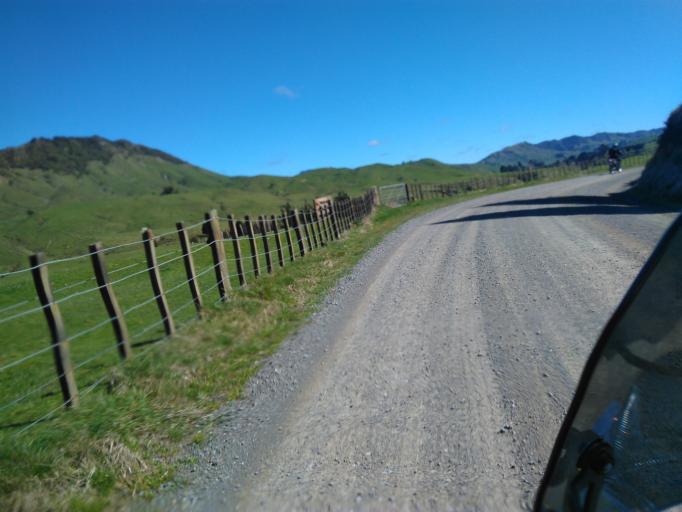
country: NZ
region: Bay of Plenty
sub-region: Opotiki District
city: Opotiki
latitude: -38.3088
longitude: 177.5630
